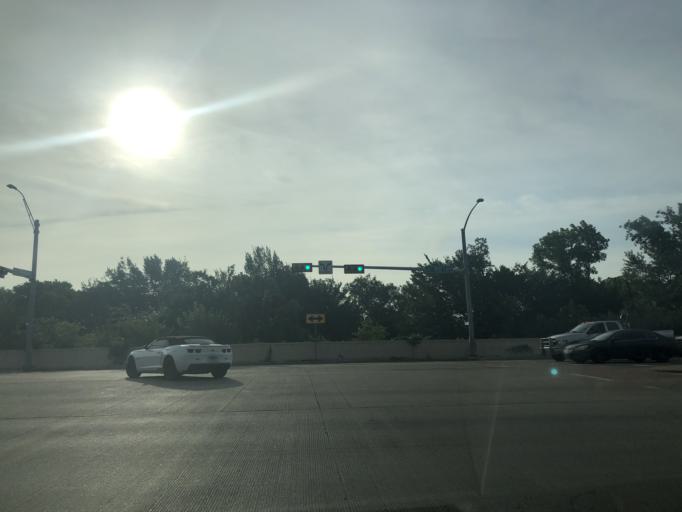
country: US
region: Texas
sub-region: Dallas County
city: Grand Prairie
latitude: 32.7923
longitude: -96.9948
